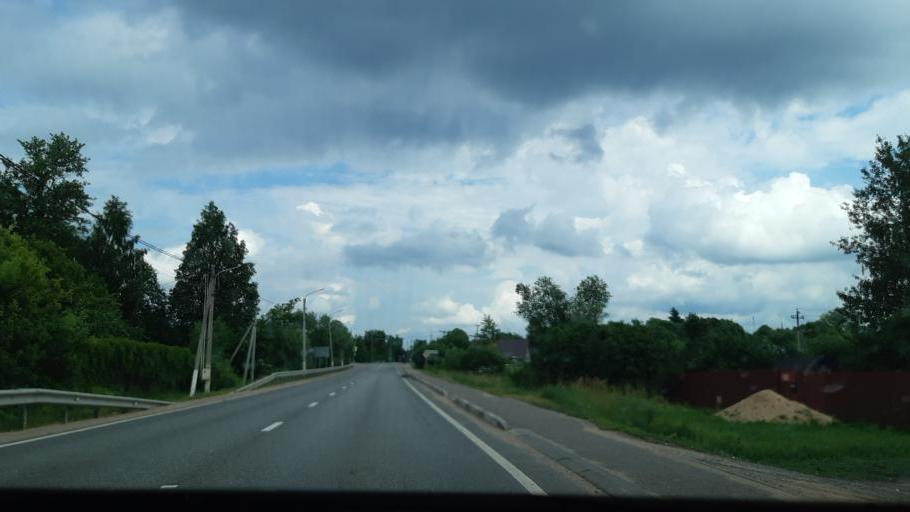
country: RU
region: Moskovskaya
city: Dorokhovo
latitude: 55.5407
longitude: 36.3639
